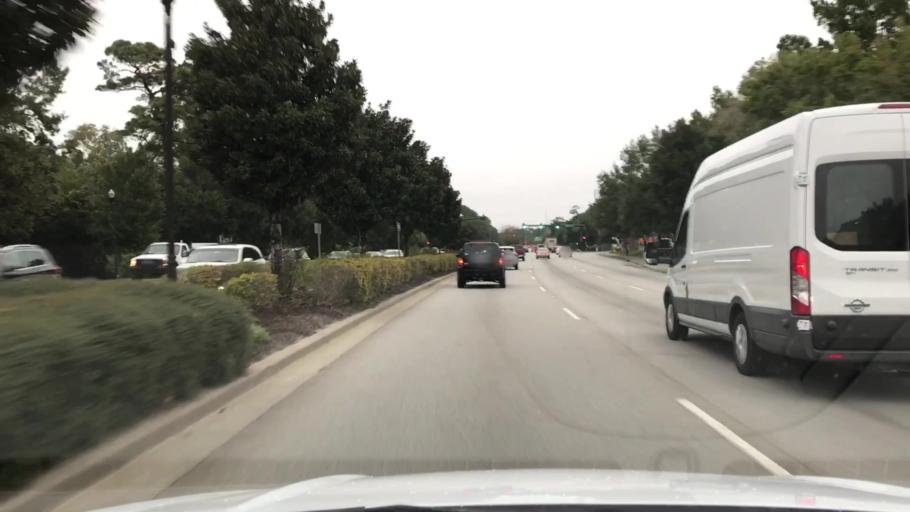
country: US
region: South Carolina
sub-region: Charleston County
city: Mount Pleasant
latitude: 32.8301
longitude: -79.8330
